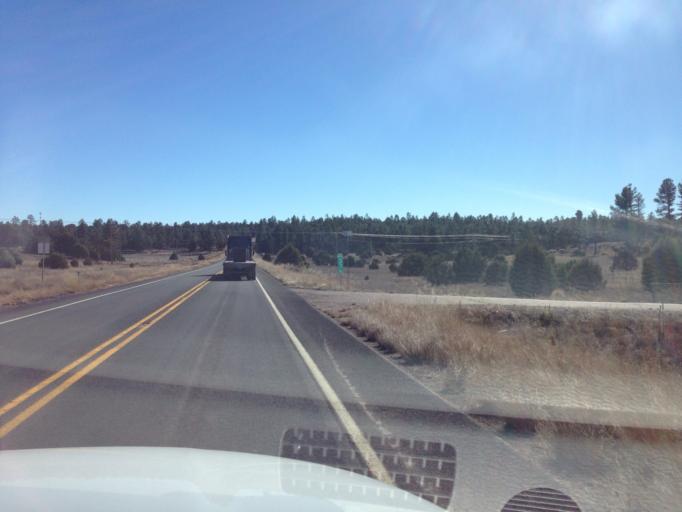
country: US
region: Arizona
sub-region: Navajo County
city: Linden
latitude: 34.2829
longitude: -110.1038
